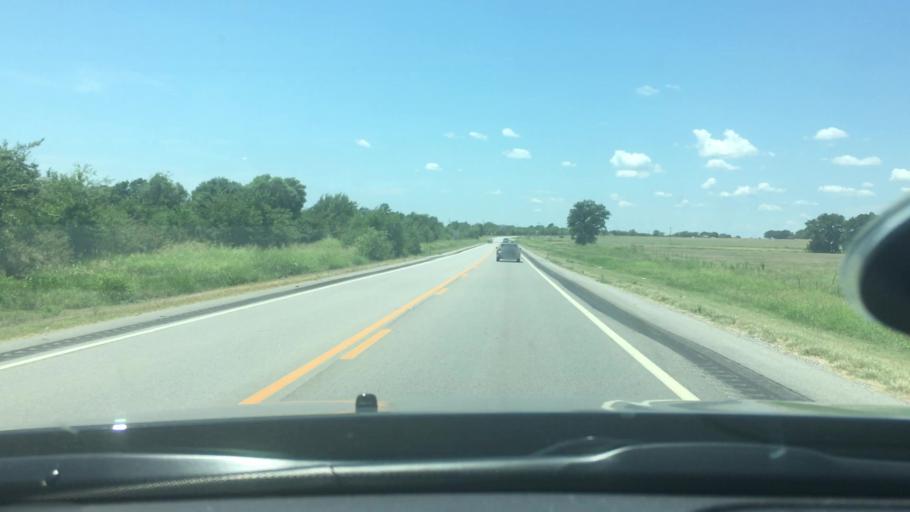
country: US
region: Oklahoma
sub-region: Bryan County
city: Durant
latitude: 34.0156
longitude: -96.1594
